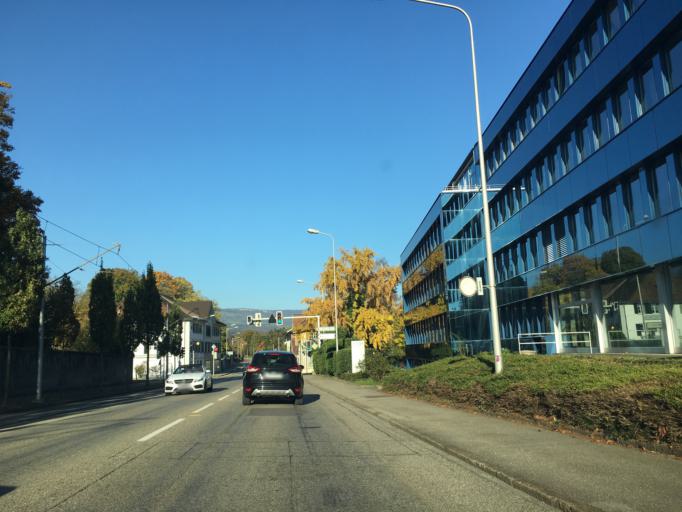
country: CH
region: Solothurn
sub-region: Bezirk Solothurn
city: Solothurn
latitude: 47.2114
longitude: 7.5443
